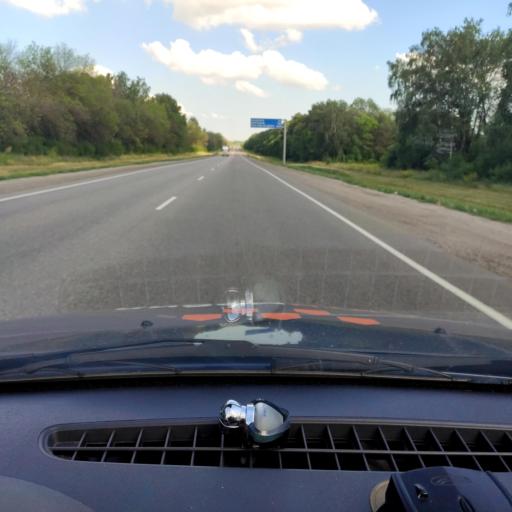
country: RU
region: Lipetsk
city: Yelets
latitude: 52.5871
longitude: 38.6119
